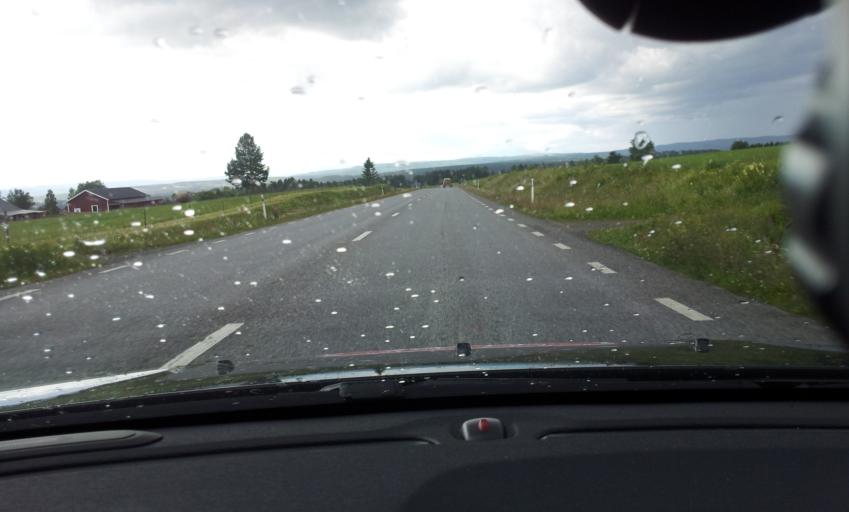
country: SE
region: Jaemtland
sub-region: Krokoms Kommun
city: Valla
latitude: 63.3044
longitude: 13.8844
